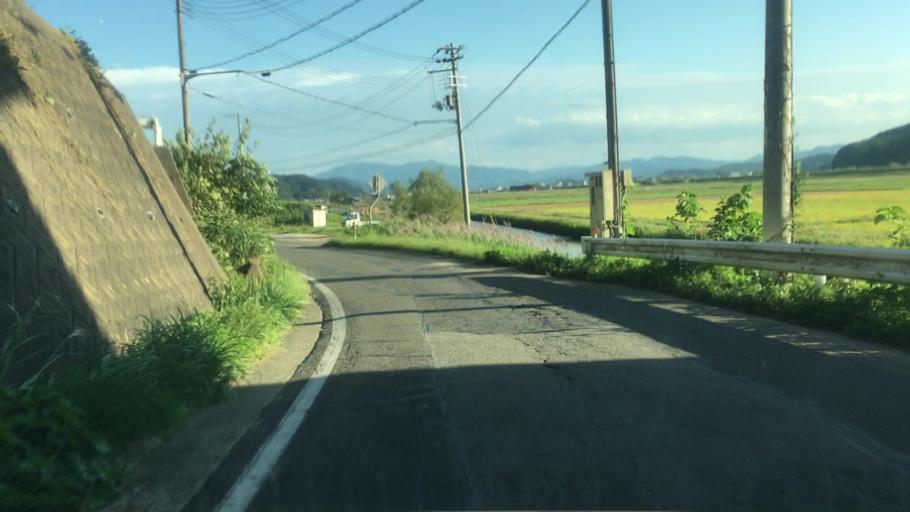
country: JP
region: Hyogo
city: Toyooka
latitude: 35.5871
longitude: 134.8049
